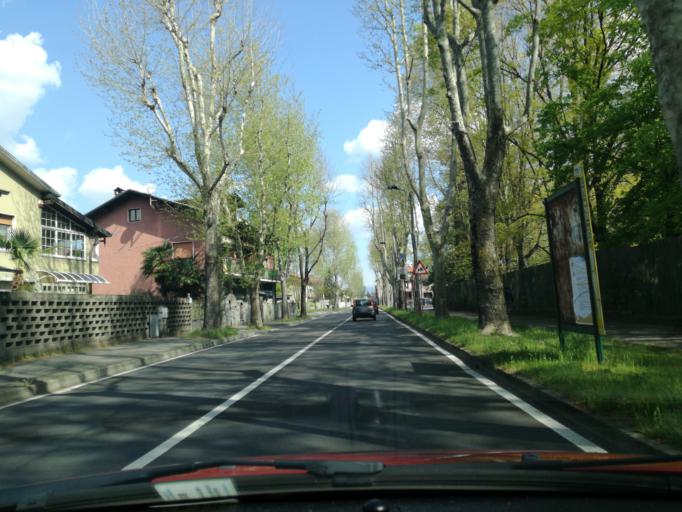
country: IT
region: Lombardy
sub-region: Provincia di Monza e Brianza
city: Limbiate
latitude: 45.5919
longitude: 9.1271
